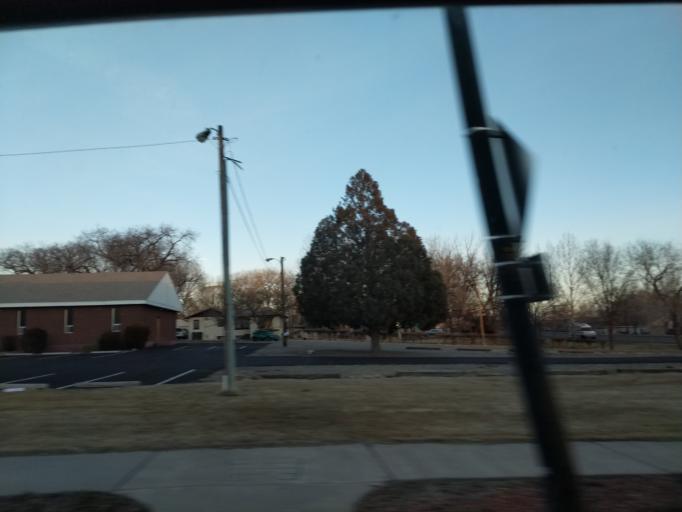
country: US
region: Colorado
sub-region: Mesa County
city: Grand Junction
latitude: 39.0995
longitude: -108.5523
